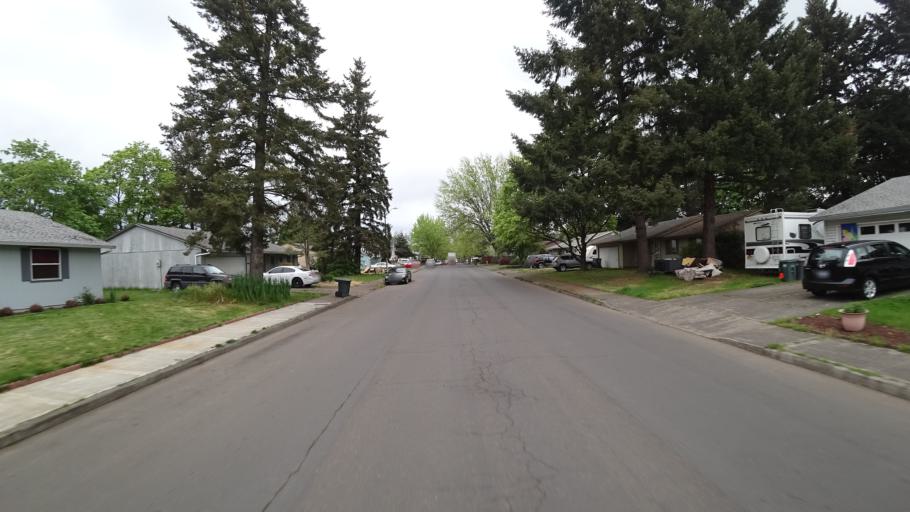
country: US
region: Oregon
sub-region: Washington County
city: Hillsboro
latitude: 45.5392
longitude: -122.9728
